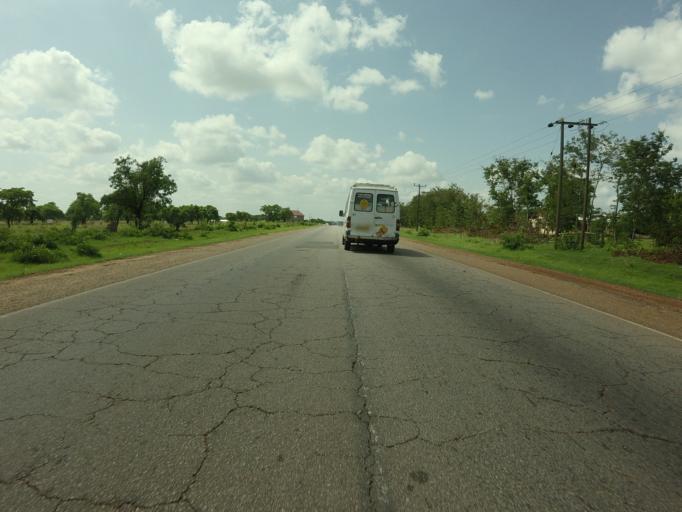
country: GH
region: Northern
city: Savelugu
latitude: 9.5915
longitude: -0.8323
